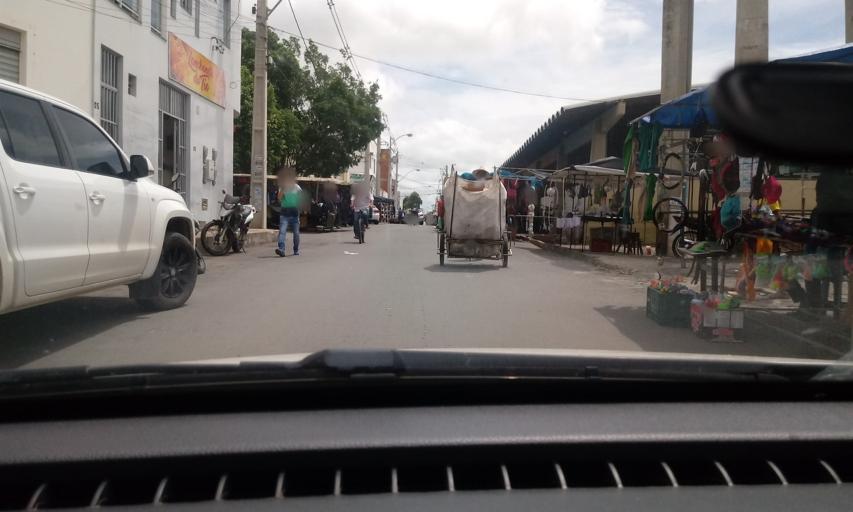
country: BR
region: Bahia
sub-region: Guanambi
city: Guanambi
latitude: -14.2288
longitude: -42.7789
